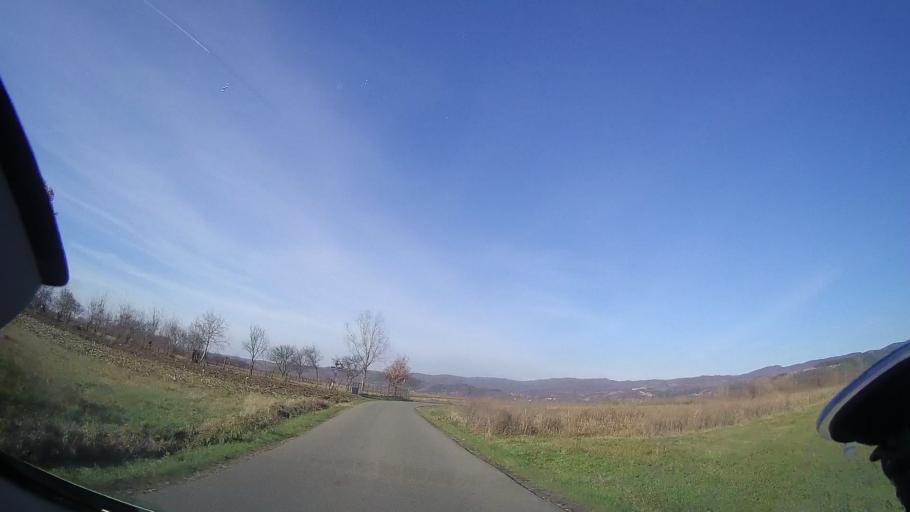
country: RO
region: Bihor
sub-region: Comuna Auseu
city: Auseu
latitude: 47.0258
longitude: 22.4862
